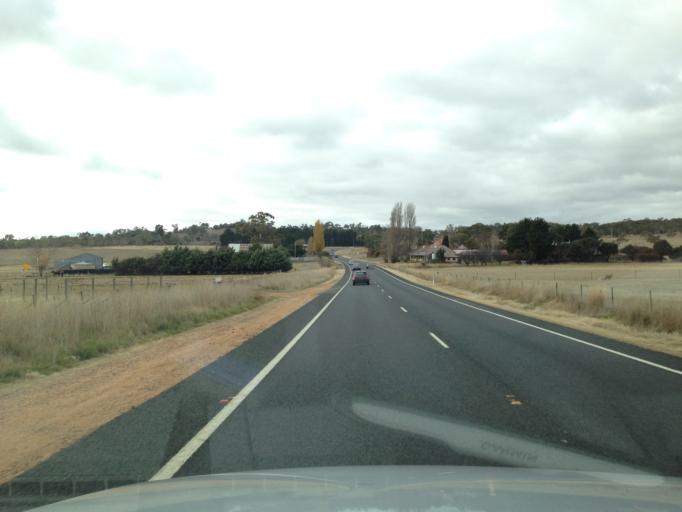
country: AU
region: New South Wales
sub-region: Cooma-Monaro
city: Cooma
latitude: -36.2437
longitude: 149.0600
